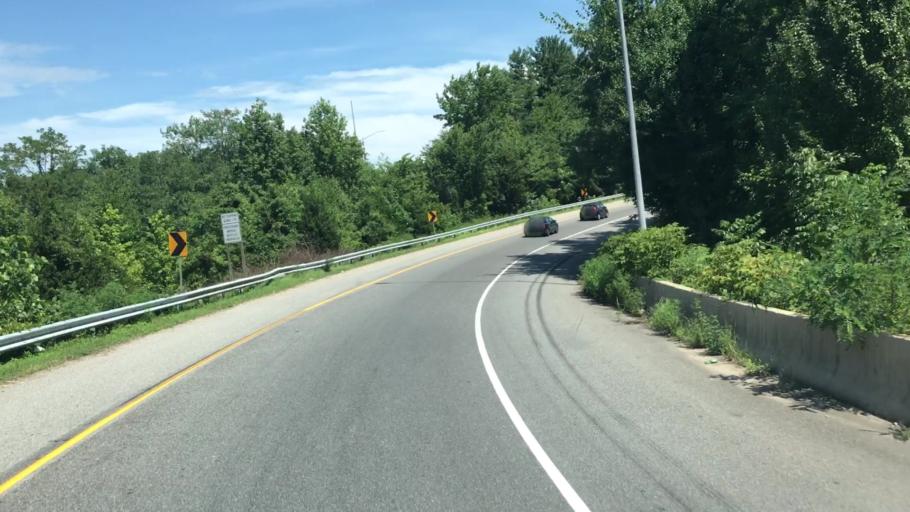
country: US
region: Maryland
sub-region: Prince George's County
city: Camp Springs
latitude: 38.8172
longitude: -76.9159
